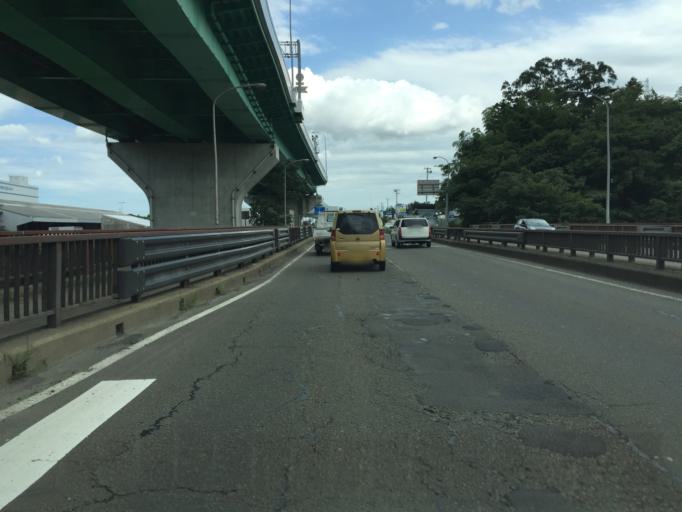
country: JP
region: Miyagi
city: Sendai
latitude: 38.2155
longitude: 140.8124
